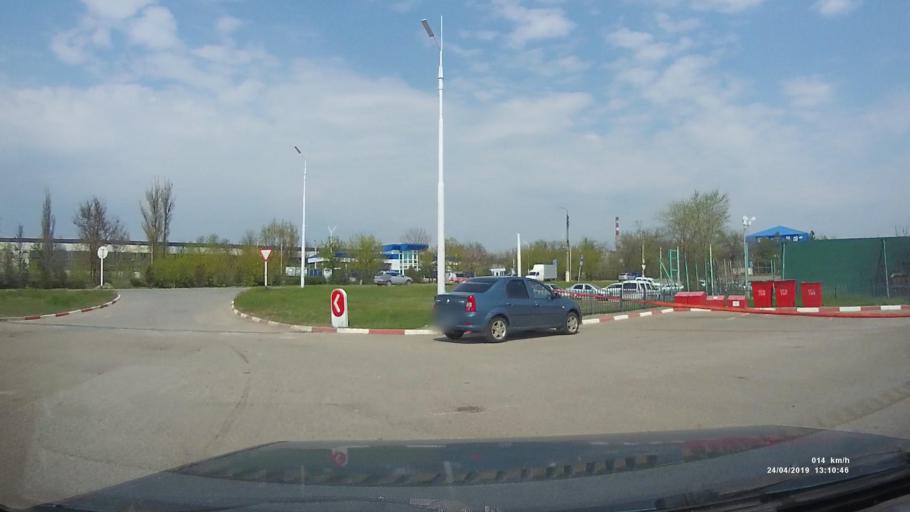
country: RU
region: Kalmykiya
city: Elista
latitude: 46.3116
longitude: 44.2928
